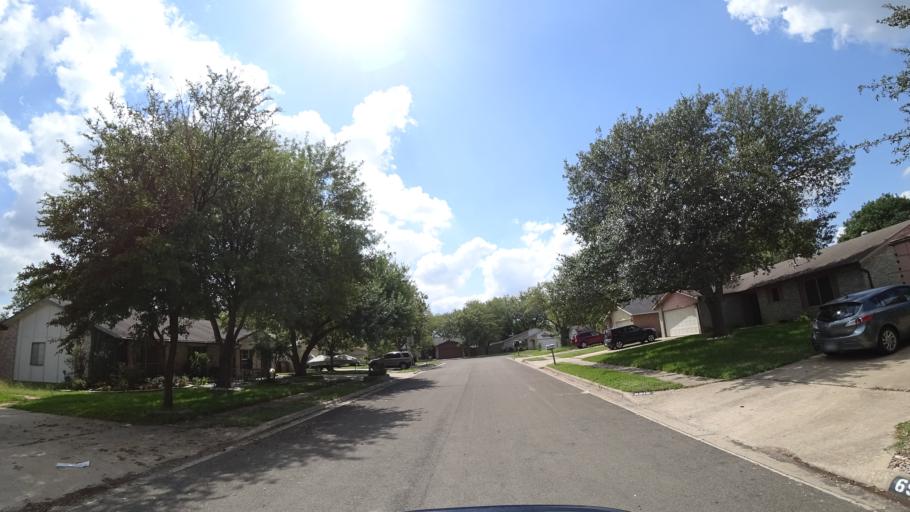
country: US
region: Texas
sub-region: Travis County
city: Onion Creek
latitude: 30.1912
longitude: -97.7836
